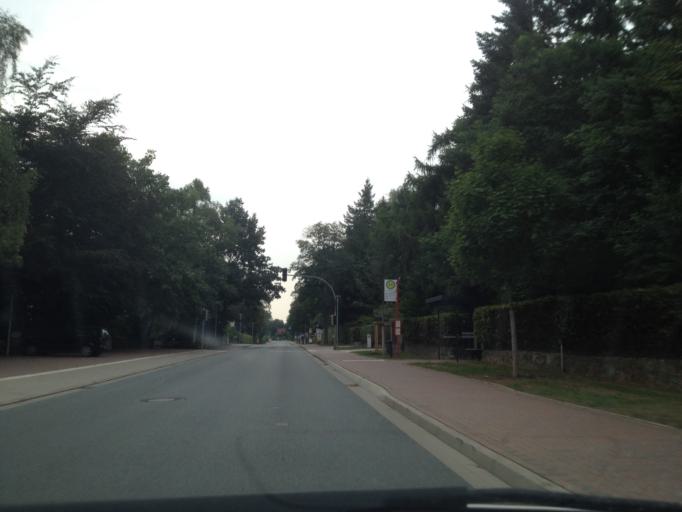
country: DE
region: Schleswig-Holstein
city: Rickling
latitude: 54.0033
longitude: 10.1666
